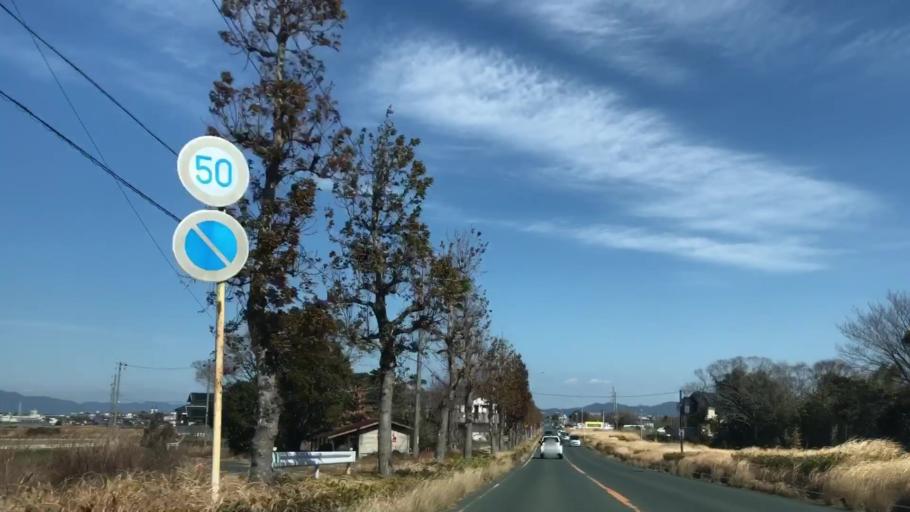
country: JP
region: Aichi
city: Toyohashi
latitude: 34.7147
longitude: 137.3629
